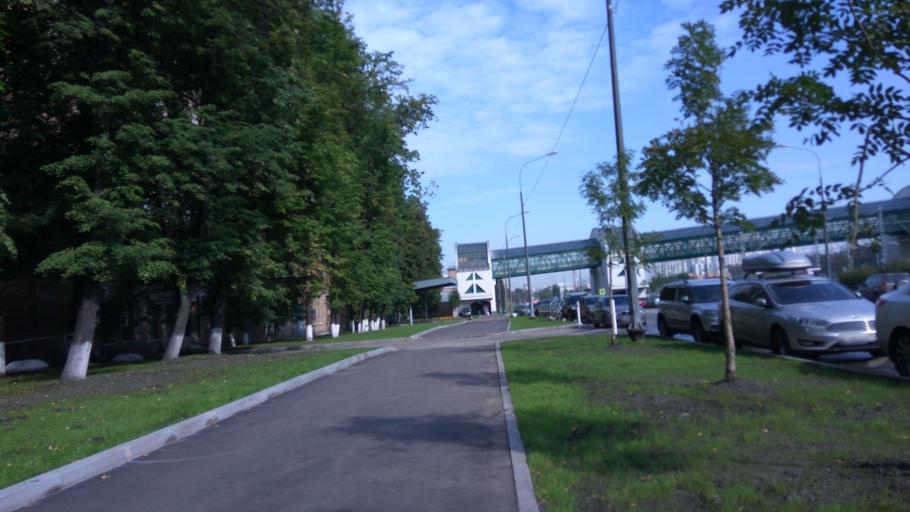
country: RU
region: Moscow
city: Lefortovo
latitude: 55.7757
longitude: 37.7435
